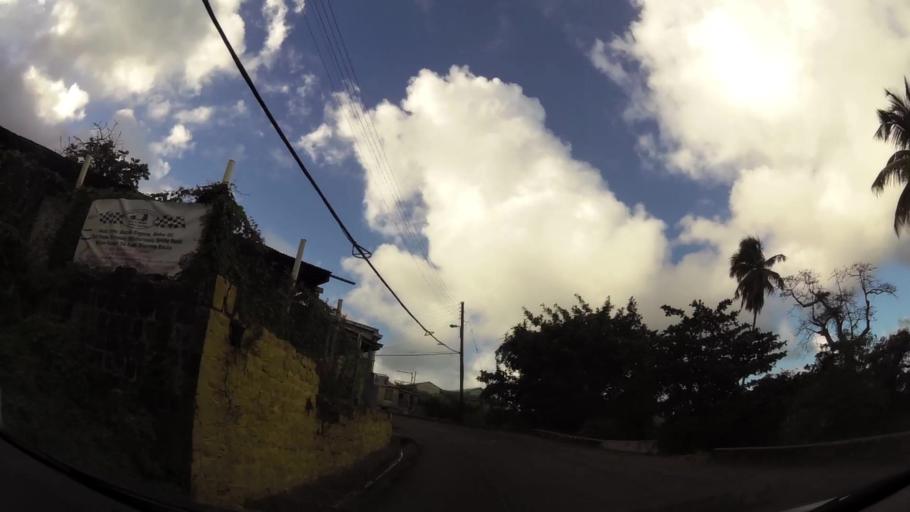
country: KN
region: Saint Mary Cayon
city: Cayon
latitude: 17.3497
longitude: -62.7304
